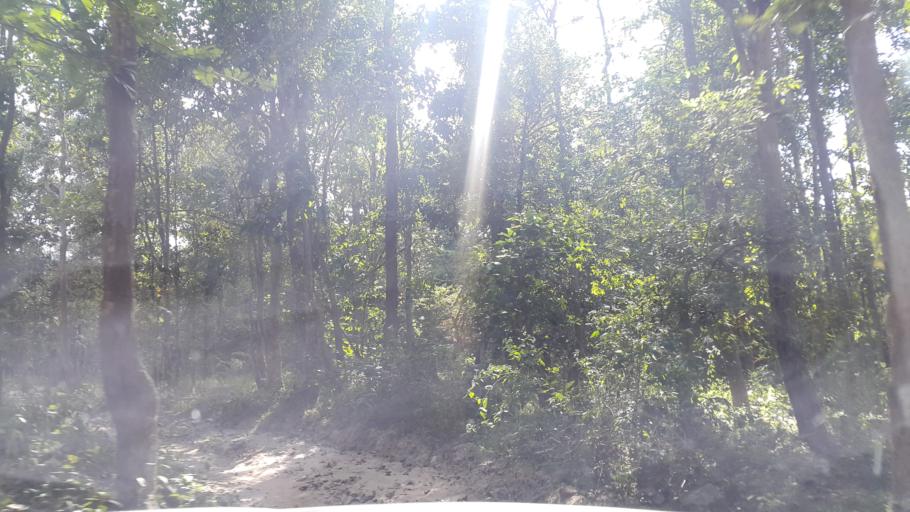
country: TH
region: Lamphun
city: Ban Thi
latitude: 18.5818
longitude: 99.1636
